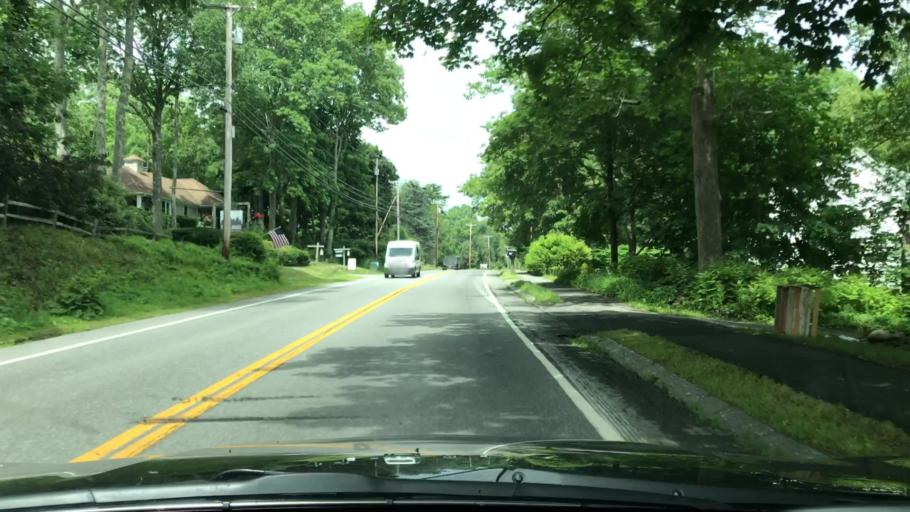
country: US
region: Maine
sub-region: Knox County
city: Camden
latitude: 44.2237
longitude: -69.0515
